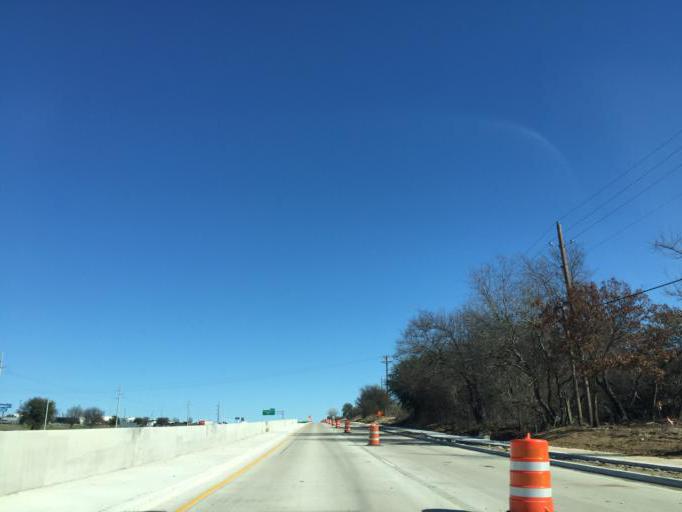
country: US
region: Texas
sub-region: Parker County
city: Hudson Oaks
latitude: 32.7518
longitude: -97.7140
